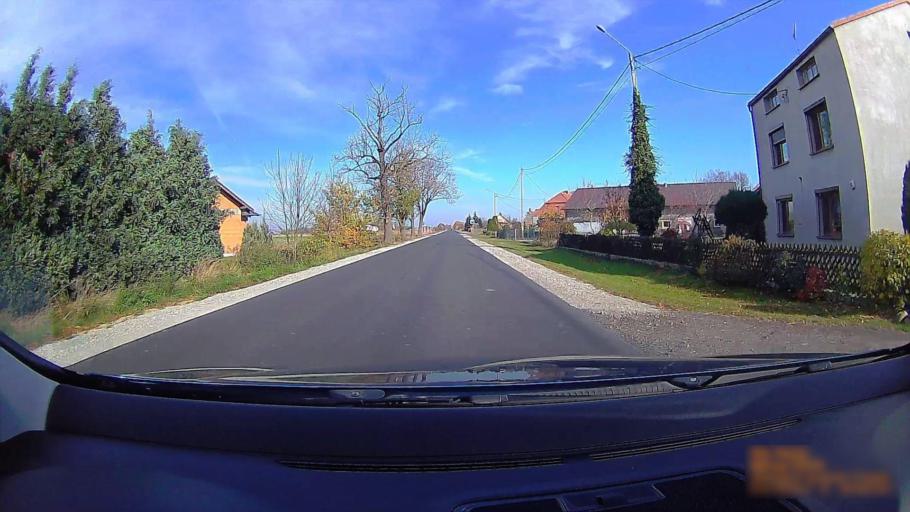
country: PL
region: Greater Poland Voivodeship
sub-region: Powiat ostrzeszowski
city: Doruchow
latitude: 51.4036
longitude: 18.0676
